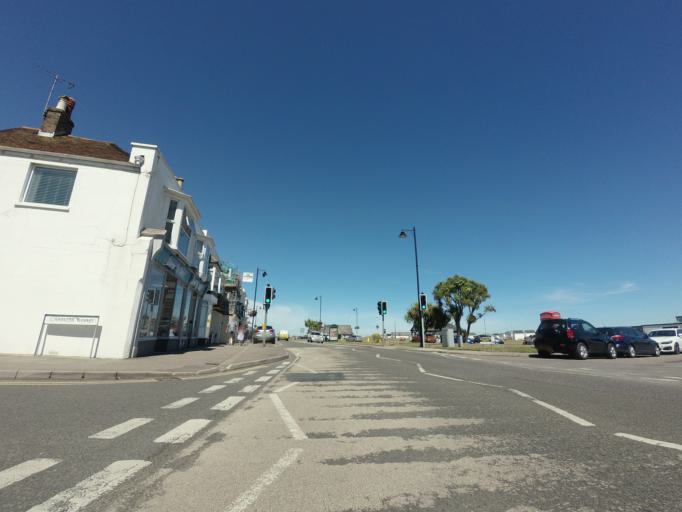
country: GB
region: England
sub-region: Kent
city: Deal
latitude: 51.2123
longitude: 1.4023
